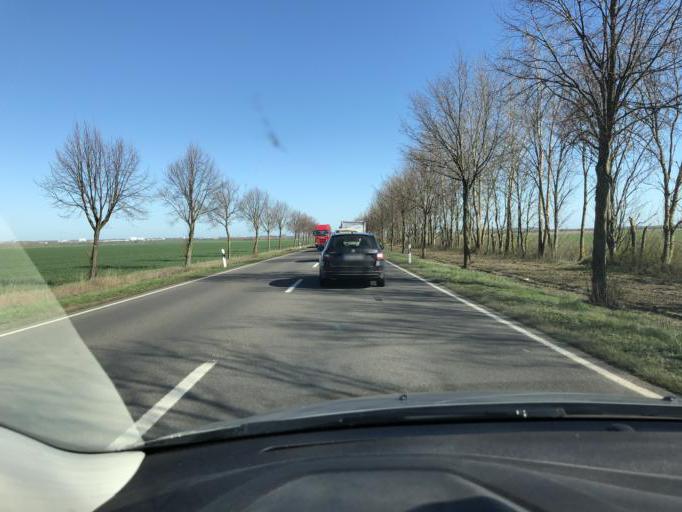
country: DE
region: Saxony-Anhalt
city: Welsleben
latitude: 52.0137
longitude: 11.6069
